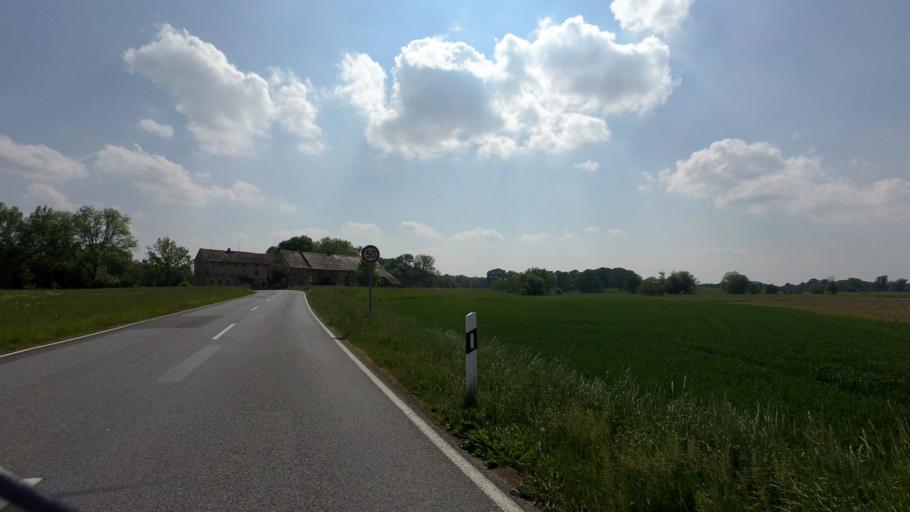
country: DE
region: Saxony
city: Hochkirch
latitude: 51.2016
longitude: 14.6032
